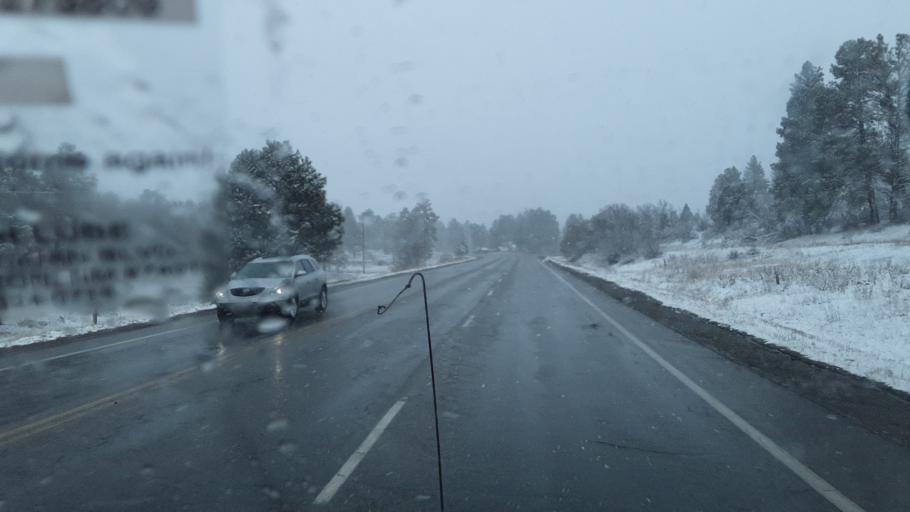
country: US
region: Colorado
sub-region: Archuleta County
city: Pagosa Springs
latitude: 37.2711
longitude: -107.0317
